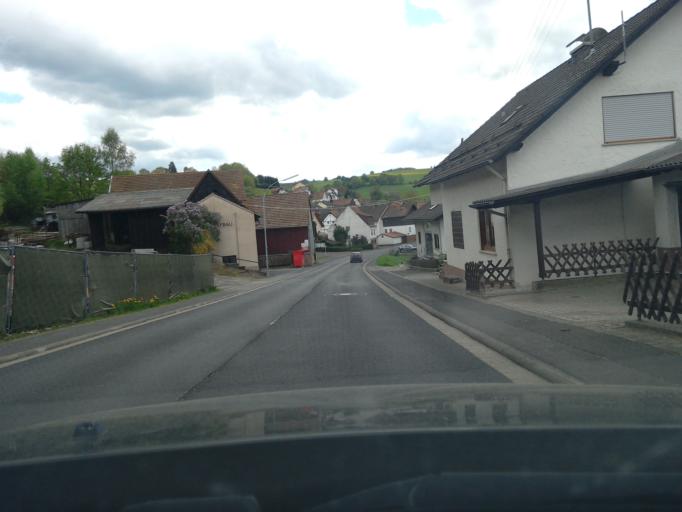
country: DE
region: Bavaria
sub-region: Regierungsbezirk Unterfranken
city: Aura im Sinngrund
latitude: 50.1714
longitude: 9.4748
